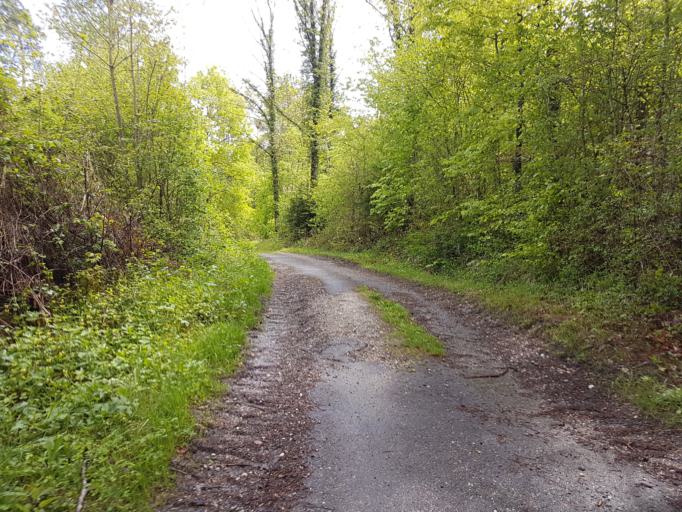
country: CH
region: Vaud
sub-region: Ouest Lausannois District
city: Bussigny
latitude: 46.5518
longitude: 6.5340
